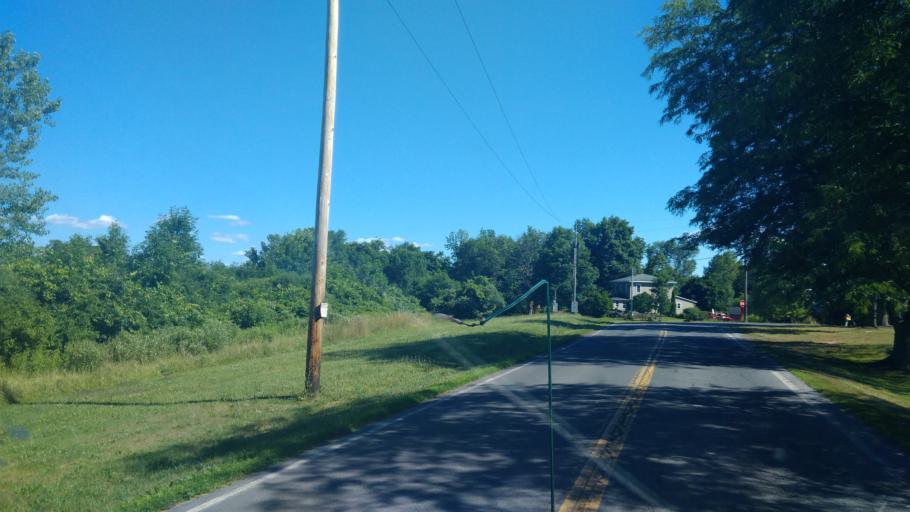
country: US
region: New York
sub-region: Seneca County
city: Seneca Falls
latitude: 42.9944
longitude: -76.8062
